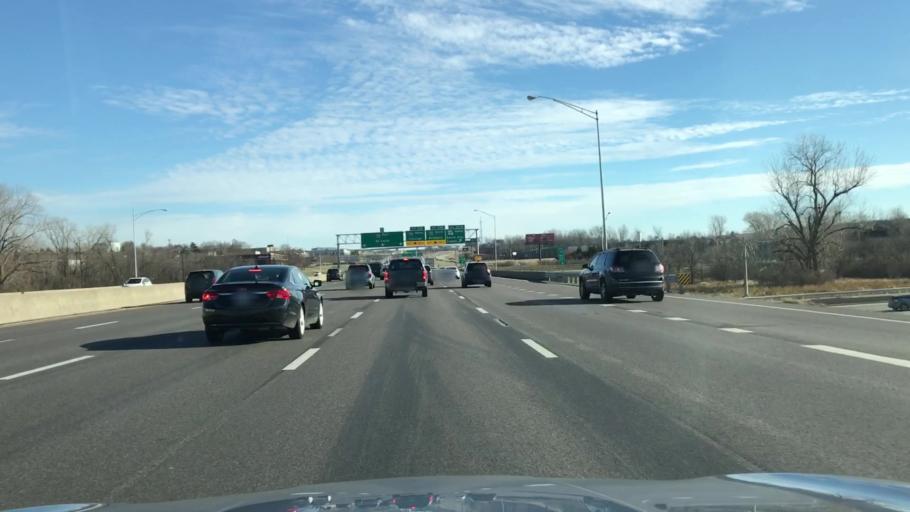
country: US
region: Missouri
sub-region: Saint Charles County
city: Saint Charles
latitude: 38.7557
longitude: -90.4599
